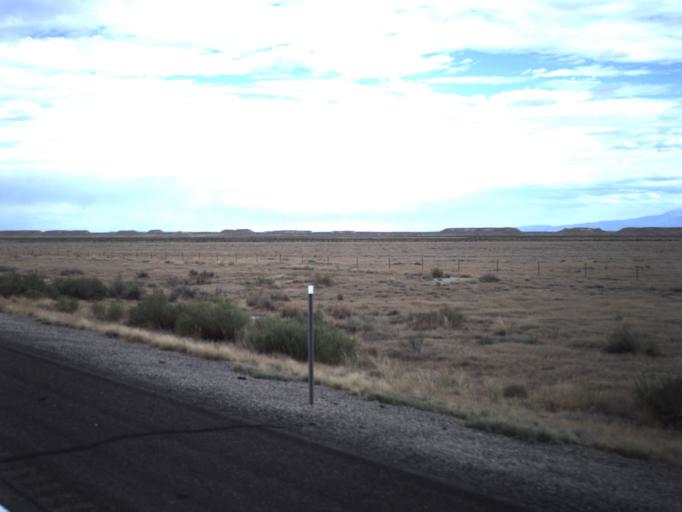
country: US
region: Utah
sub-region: Grand County
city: Moab
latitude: 38.9480
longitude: -109.7843
